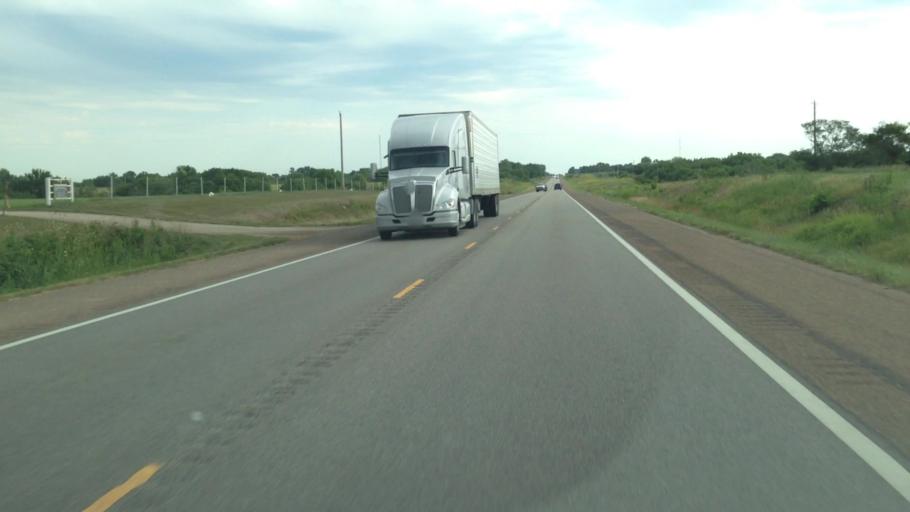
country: US
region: Kansas
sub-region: Woodson County
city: Yates Center
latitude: 38.0009
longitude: -95.7389
